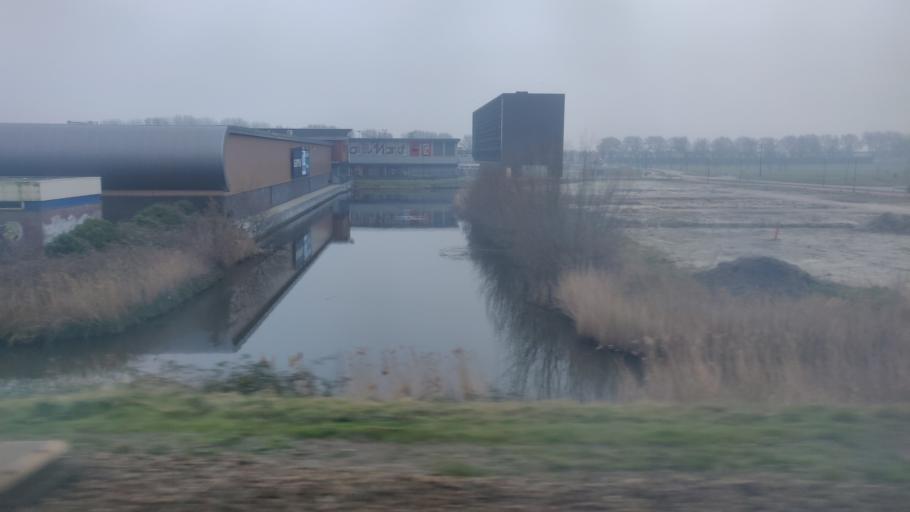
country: NL
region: North Holland
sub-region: Gemeente Langedijk
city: Broek op Langedijk
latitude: 52.6629
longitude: 4.8072
